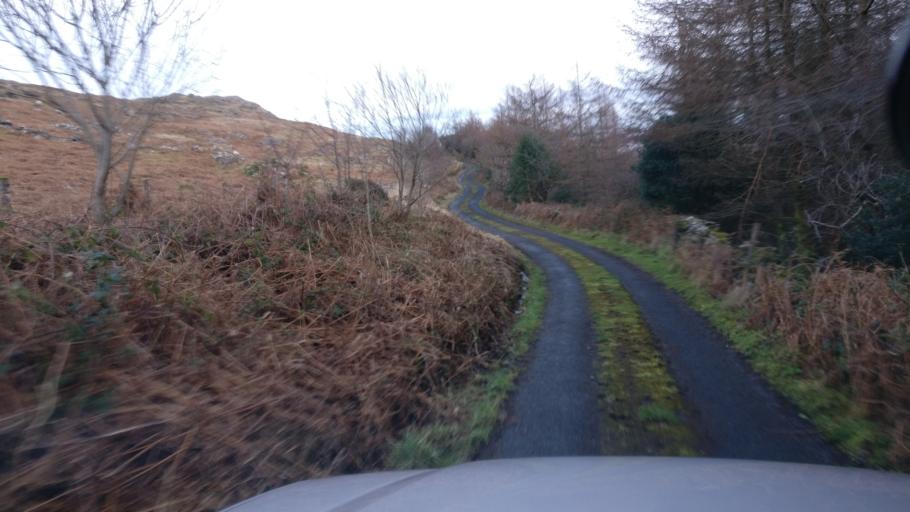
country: IE
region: Connaught
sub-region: County Galway
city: Oughterard
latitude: 53.5215
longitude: -9.4390
